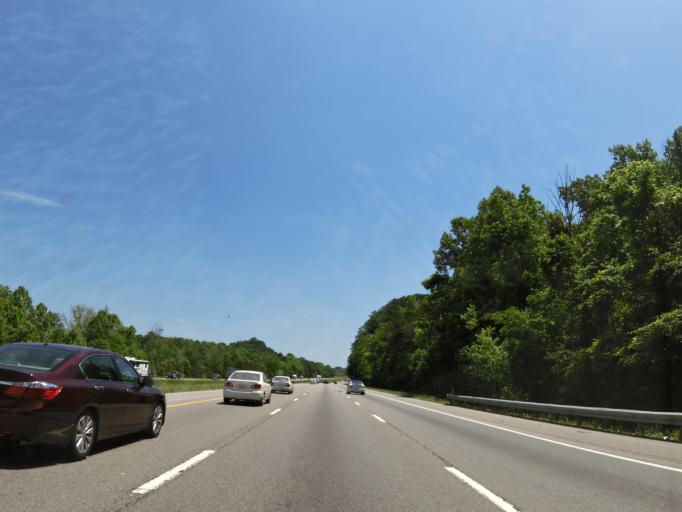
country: US
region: Tennessee
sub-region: Knox County
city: Mascot
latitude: 36.0045
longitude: -83.7598
